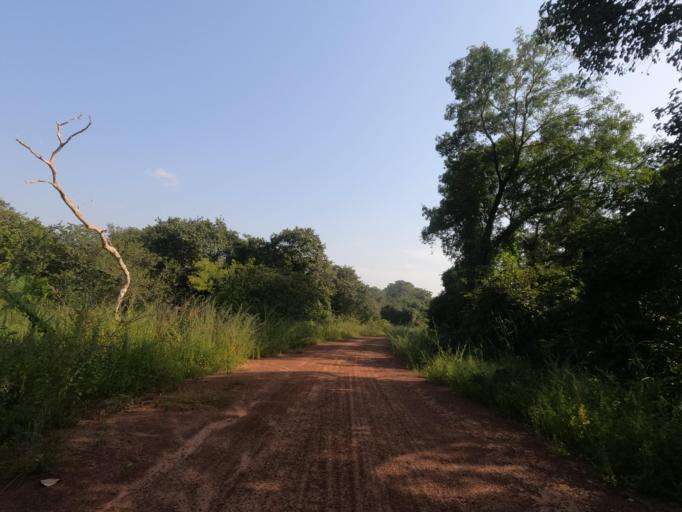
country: SN
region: Sedhiou
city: Sedhiou
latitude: 12.4401
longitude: -15.7377
